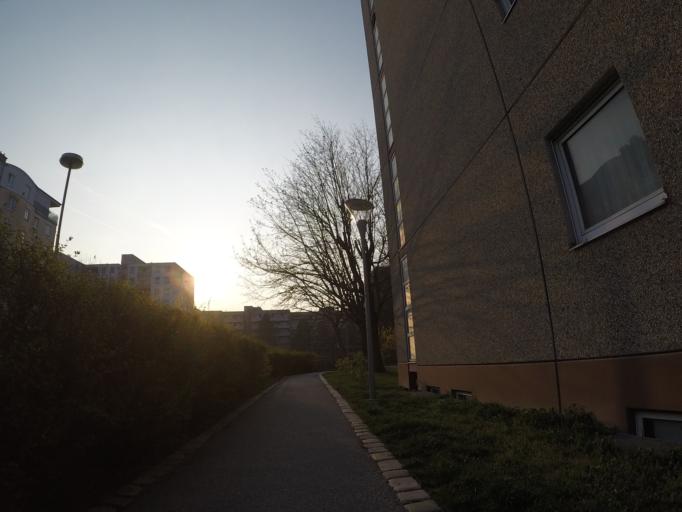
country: AT
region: Lower Austria
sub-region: Politischer Bezirk Modling
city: Wiener Neudorf
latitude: 48.0895
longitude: 16.3119
